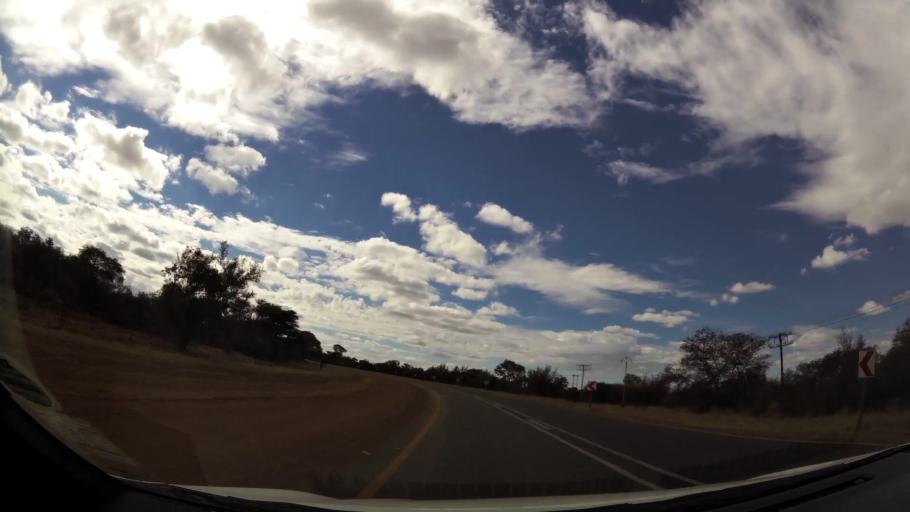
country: ZA
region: Limpopo
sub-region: Waterberg District Municipality
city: Warmbaths
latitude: -24.9015
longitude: 28.2787
